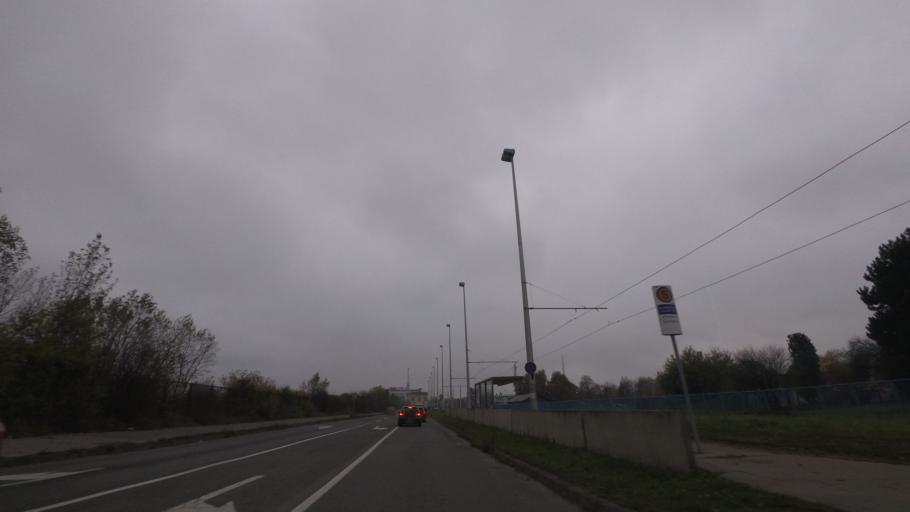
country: HR
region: Grad Zagreb
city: Dubrava
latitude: 45.7910
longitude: 16.0367
